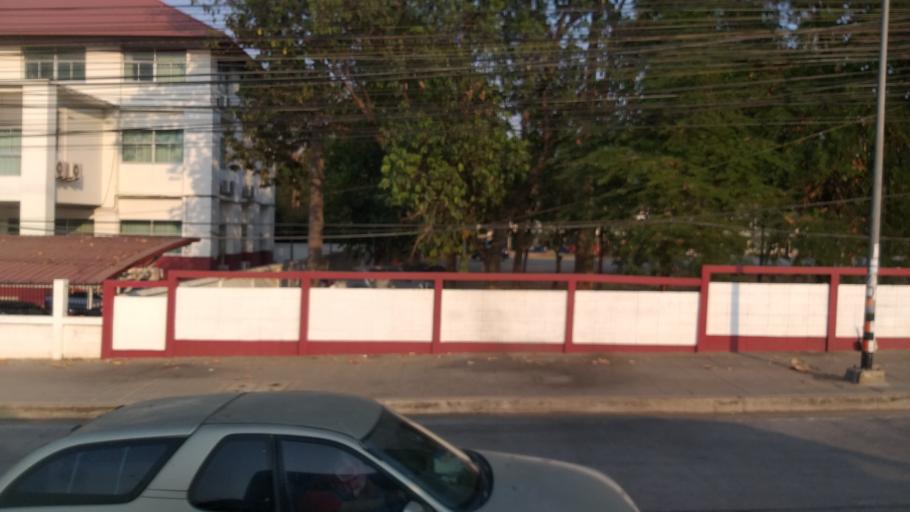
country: TH
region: Khon Kaen
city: Khon Kaen
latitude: 16.4827
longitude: 102.8328
